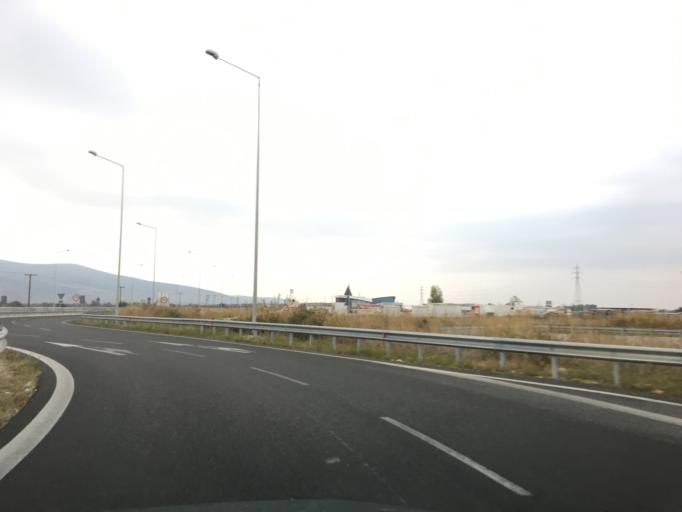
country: GR
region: Thessaly
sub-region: Trikala
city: Megalochori
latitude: 39.5663
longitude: 21.8215
